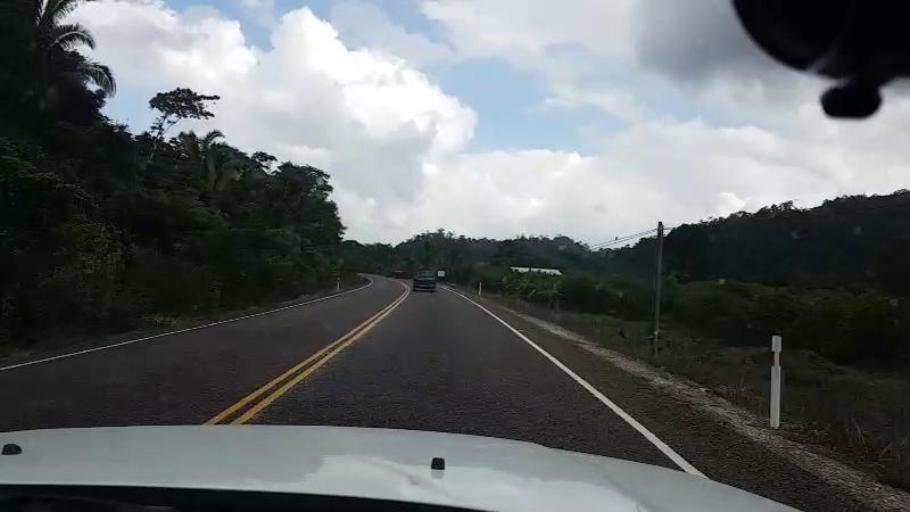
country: BZ
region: Cayo
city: Belmopan
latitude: 17.1518
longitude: -88.6691
